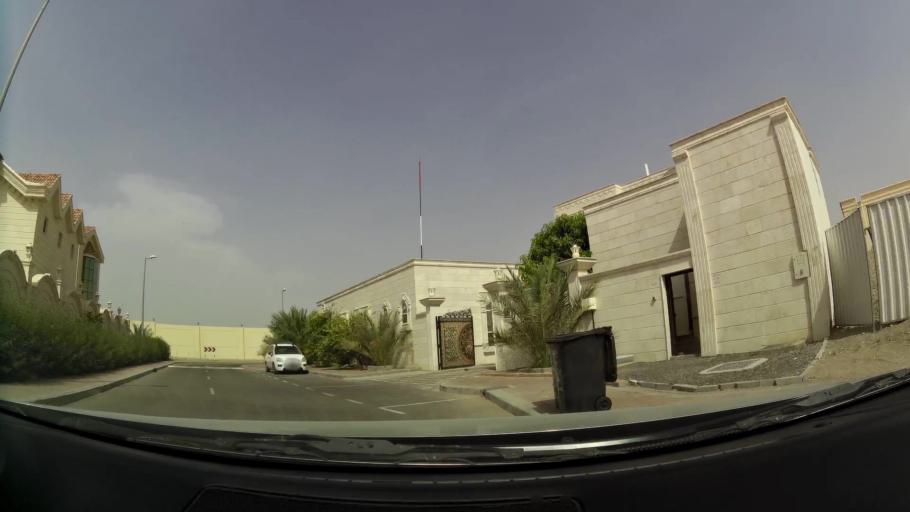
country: AE
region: Abu Dhabi
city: Al Ain
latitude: 24.1967
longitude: 55.6351
